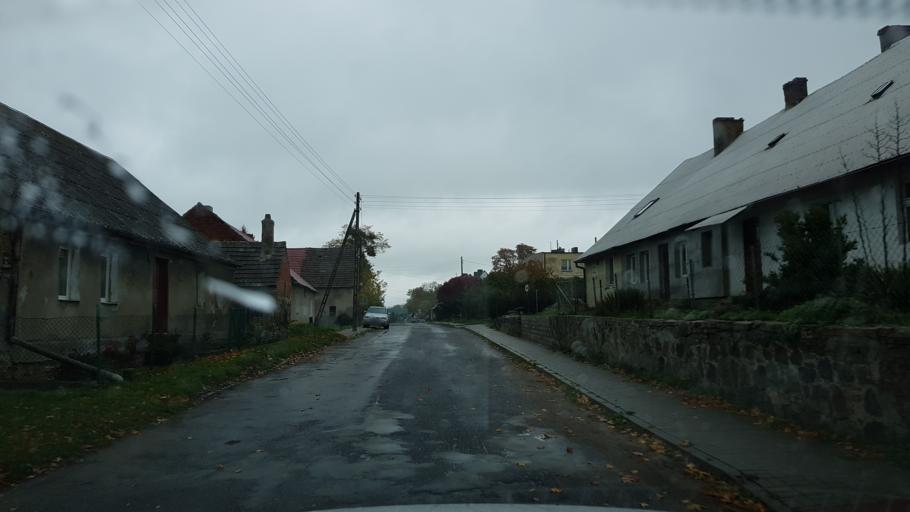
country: PL
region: West Pomeranian Voivodeship
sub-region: Powiat pyrzycki
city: Kozielice
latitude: 53.0303
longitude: 14.8514
